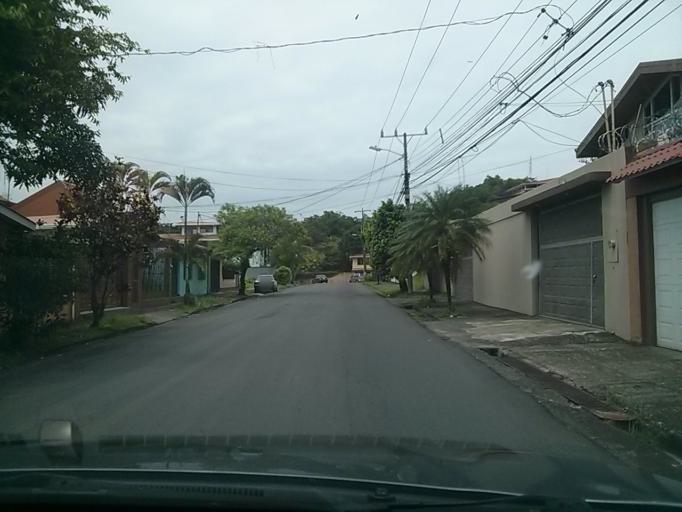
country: CR
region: Limon
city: Limon
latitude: 9.9986
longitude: -83.0356
